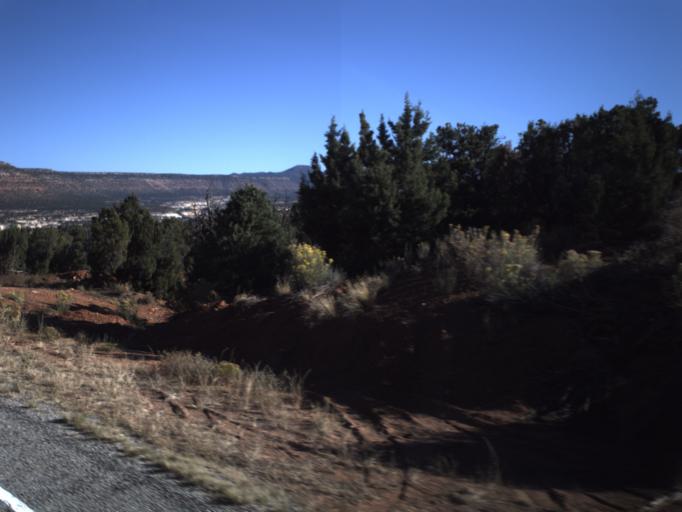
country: US
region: Utah
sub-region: San Juan County
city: Blanding
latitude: 37.5742
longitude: -110.0378
